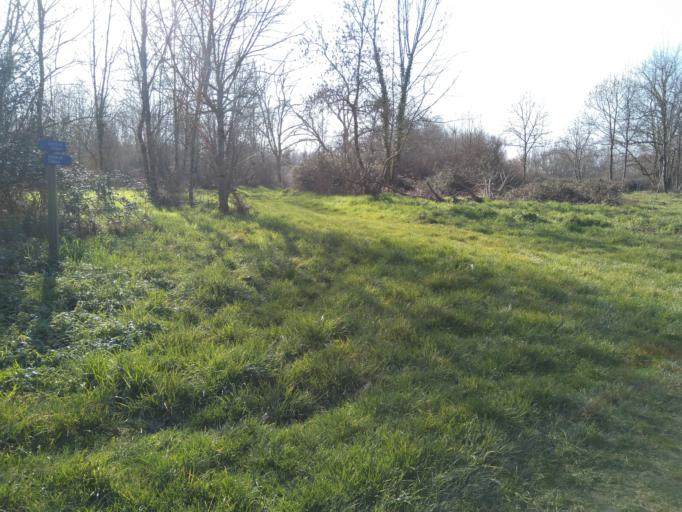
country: FR
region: Midi-Pyrenees
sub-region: Departement du Gers
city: Riscle
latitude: 43.6610
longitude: -0.1131
